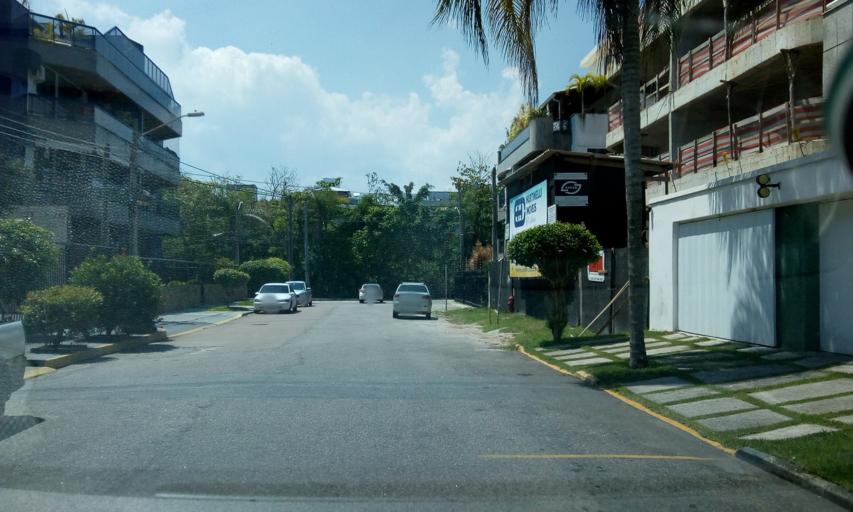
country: BR
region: Rio de Janeiro
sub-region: Nilopolis
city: Nilopolis
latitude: -23.0229
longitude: -43.4560
